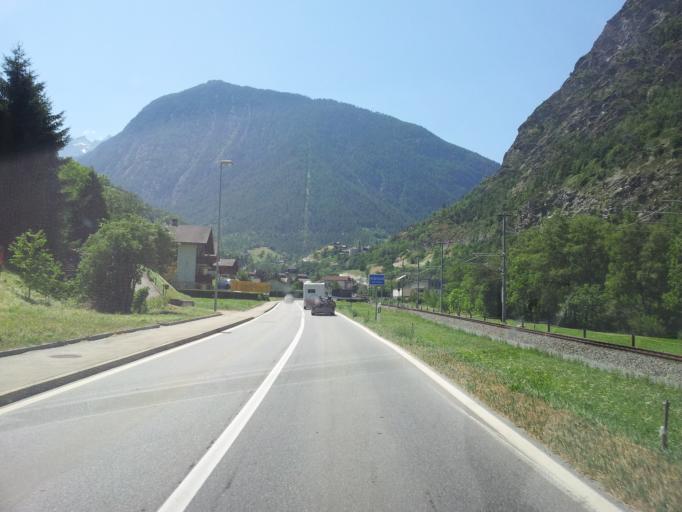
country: CH
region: Valais
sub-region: Visp District
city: Stalden
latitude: 46.2447
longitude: 7.8758
